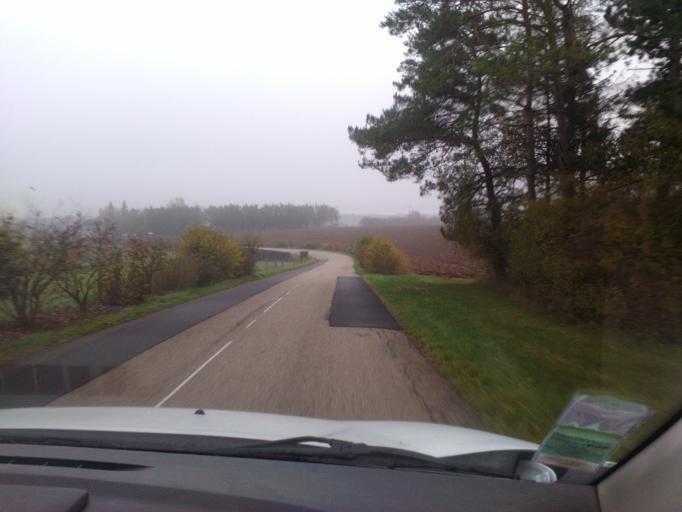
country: FR
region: Lorraine
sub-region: Departement des Vosges
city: Neufchateau
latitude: 48.3532
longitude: 5.7305
